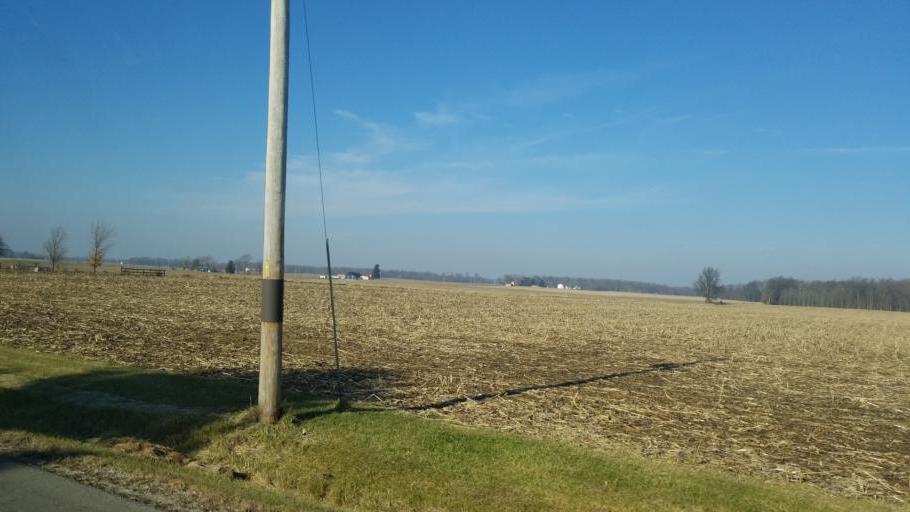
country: US
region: Ohio
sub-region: Crawford County
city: Bucyrus
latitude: 40.9067
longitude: -83.0491
